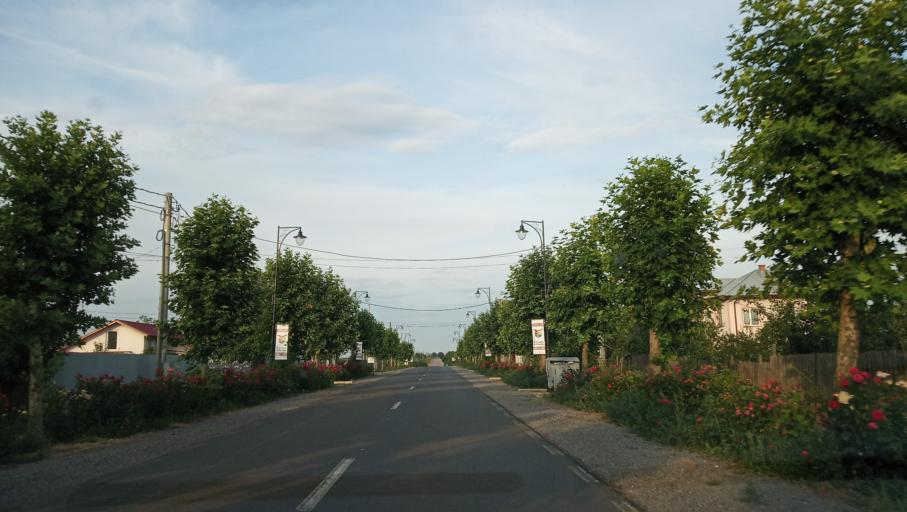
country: RO
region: Giurgiu
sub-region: Comuna Prundu
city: Prundu
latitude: 44.0969
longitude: 26.2407
